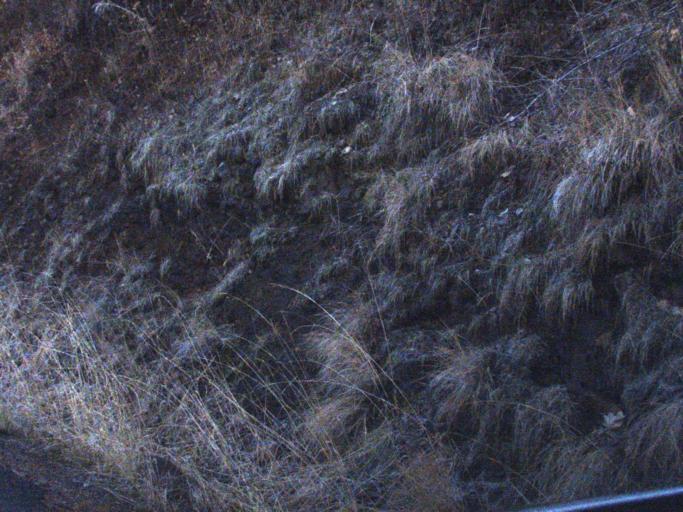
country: US
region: Washington
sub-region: Asotin County
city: Asotin
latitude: 46.0809
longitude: -117.1857
